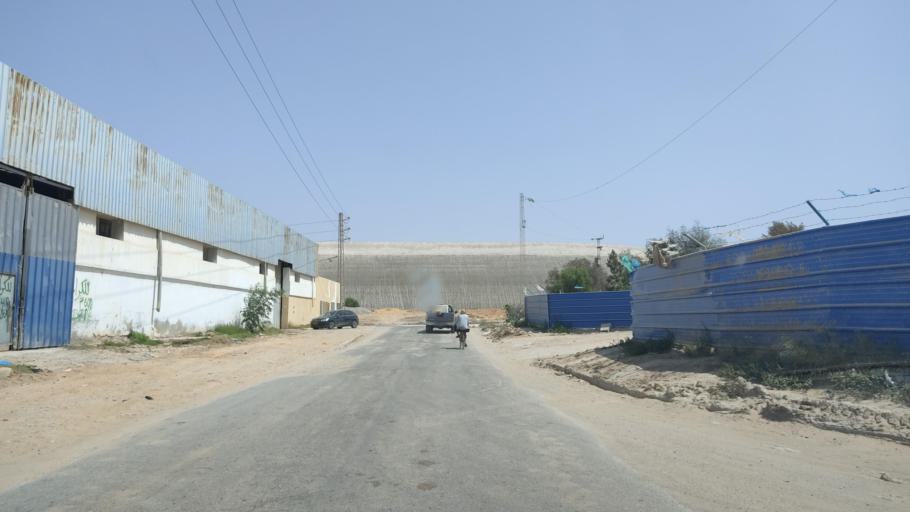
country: TN
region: Safaqis
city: Sfax
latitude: 34.6920
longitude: 10.7267
